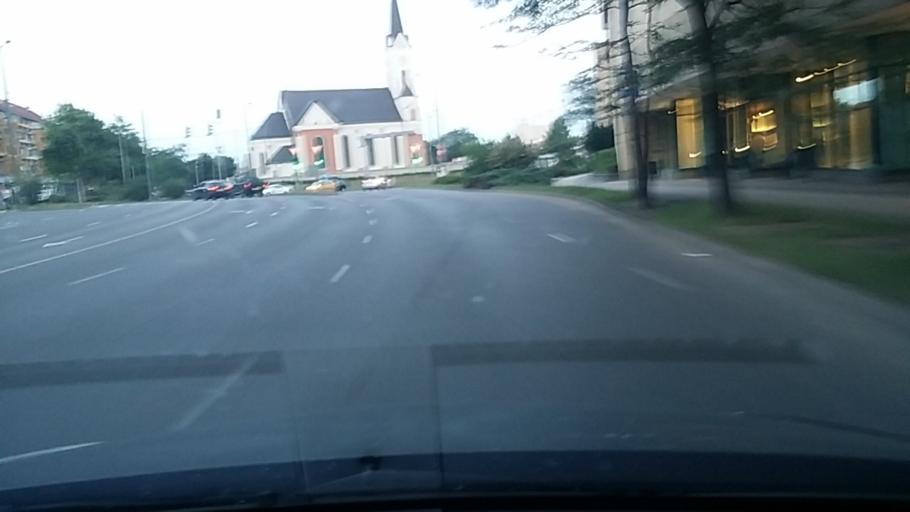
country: HU
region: Borsod-Abauj-Zemplen
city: Miskolc
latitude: 48.1070
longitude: 20.7882
